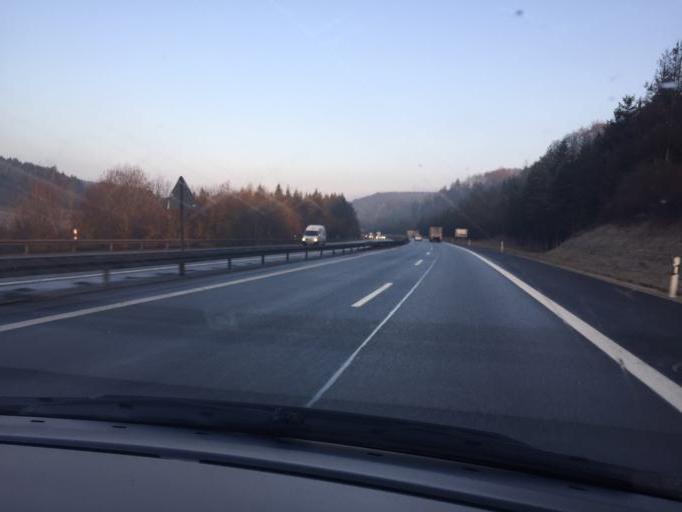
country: DE
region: Baden-Wuerttemberg
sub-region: Freiburg Region
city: Immendingen
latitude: 47.9026
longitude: 8.7003
